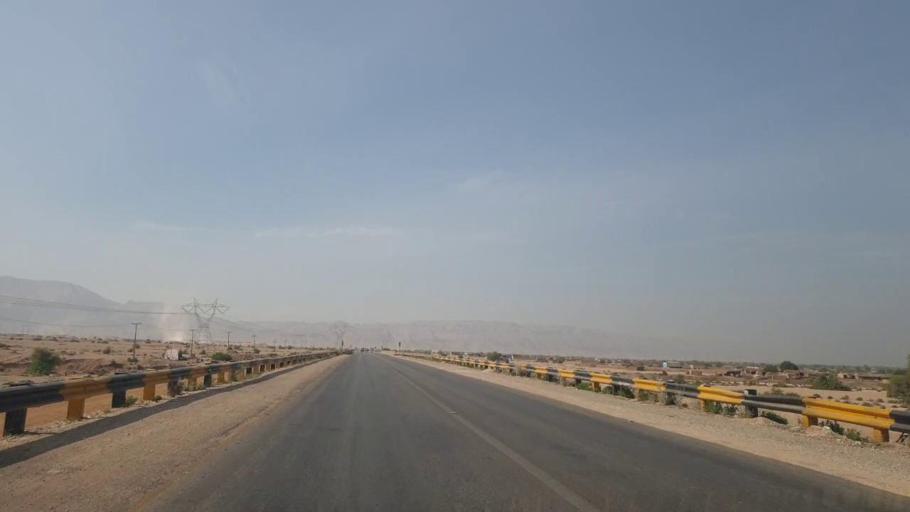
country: PK
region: Sindh
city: Sehwan
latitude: 26.2049
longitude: 67.9319
